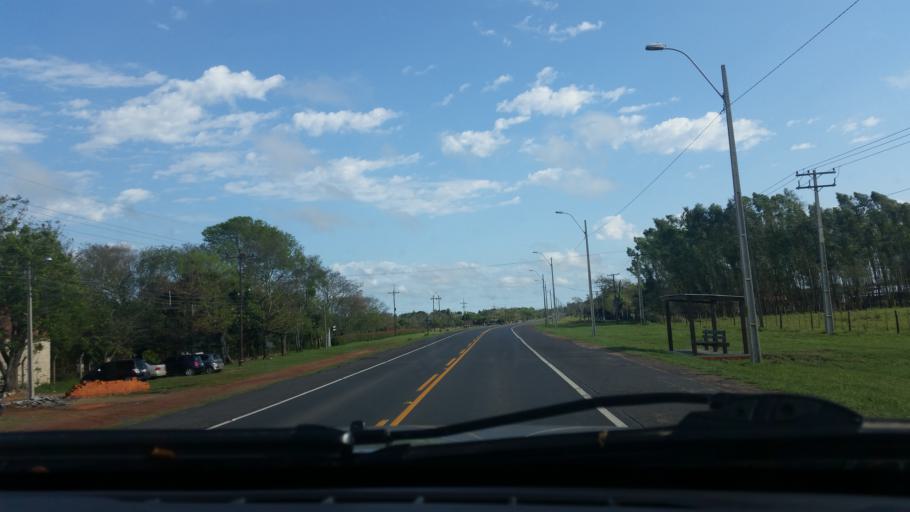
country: PY
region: Presidente Hayes
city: Villa Hayes
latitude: -25.0357
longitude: -57.5505
